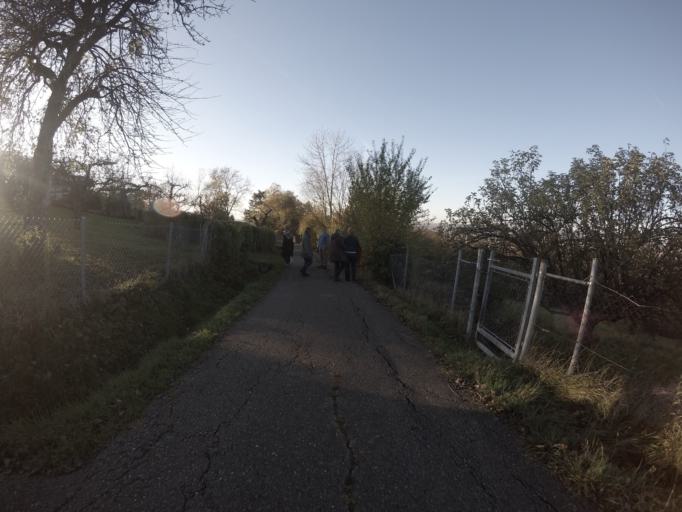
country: DE
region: Baden-Wuerttemberg
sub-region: Tuebingen Region
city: Pfullingen
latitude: 48.4751
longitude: 9.2148
